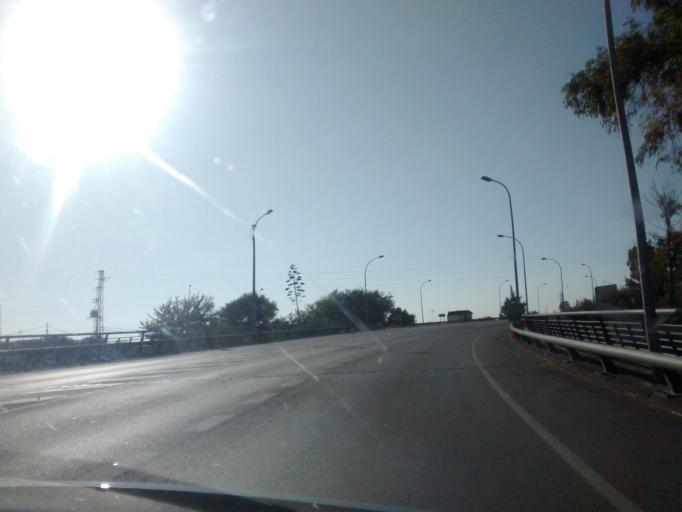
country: ES
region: Andalusia
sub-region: Provincia de Cadiz
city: Jerez de la Frontera
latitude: 36.6540
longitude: -6.0853
